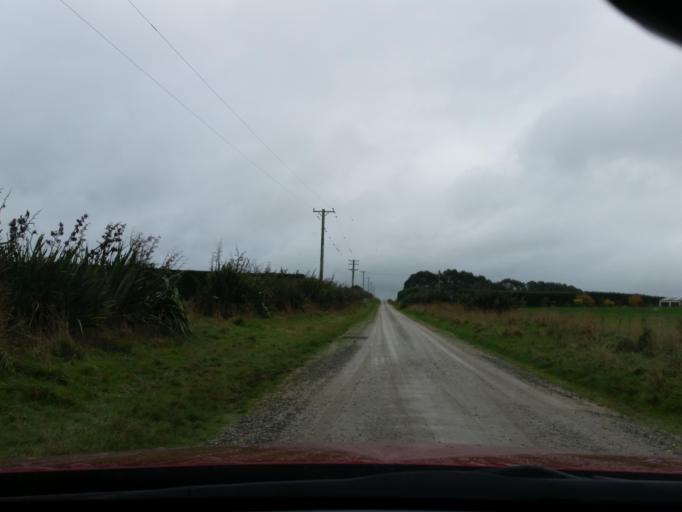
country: NZ
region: Southland
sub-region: Invercargill City
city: Invercargill
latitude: -46.2850
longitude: 168.4790
